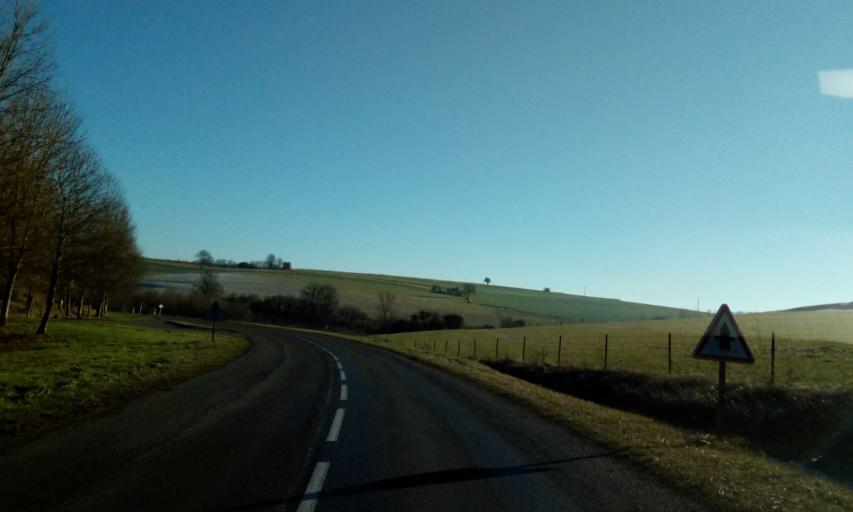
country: FR
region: Champagne-Ardenne
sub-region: Departement des Ardennes
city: Signy-le-Petit
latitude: 49.7765
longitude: 4.3830
